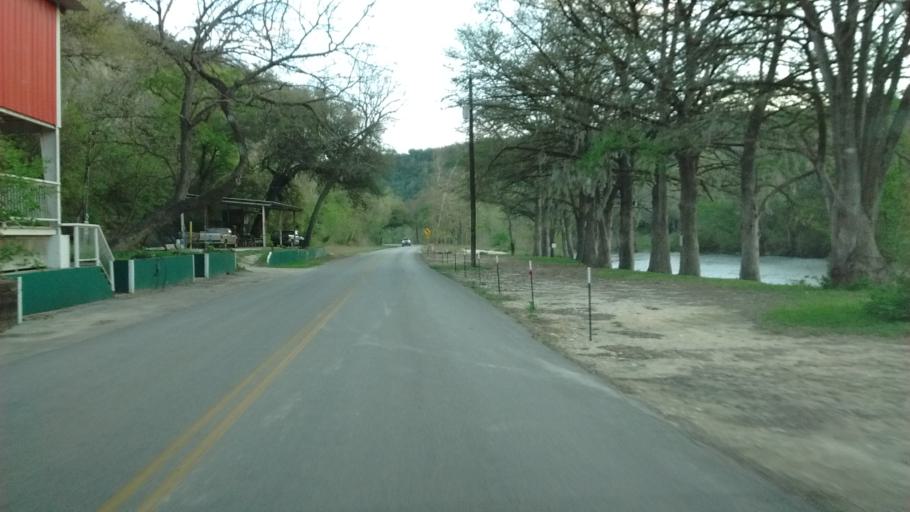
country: US
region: Texas
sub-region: Comal County
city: New Braunfels
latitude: 29.7699
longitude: -98.1584
